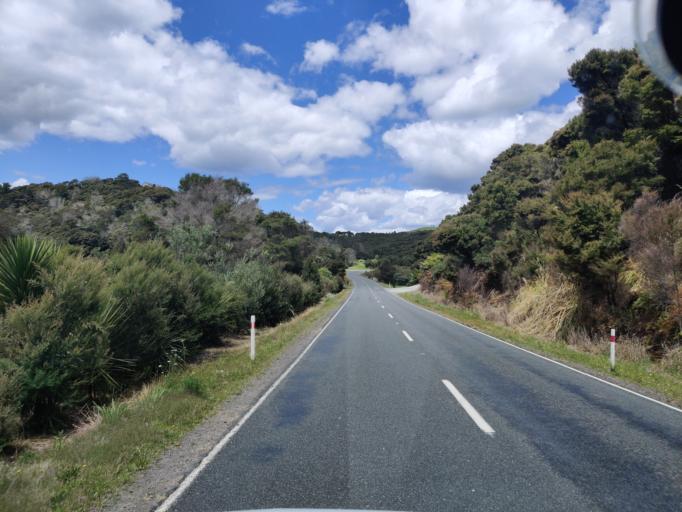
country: NZ
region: Northland
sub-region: Far North District
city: Paihia
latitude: -35.2723
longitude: 174.1375
